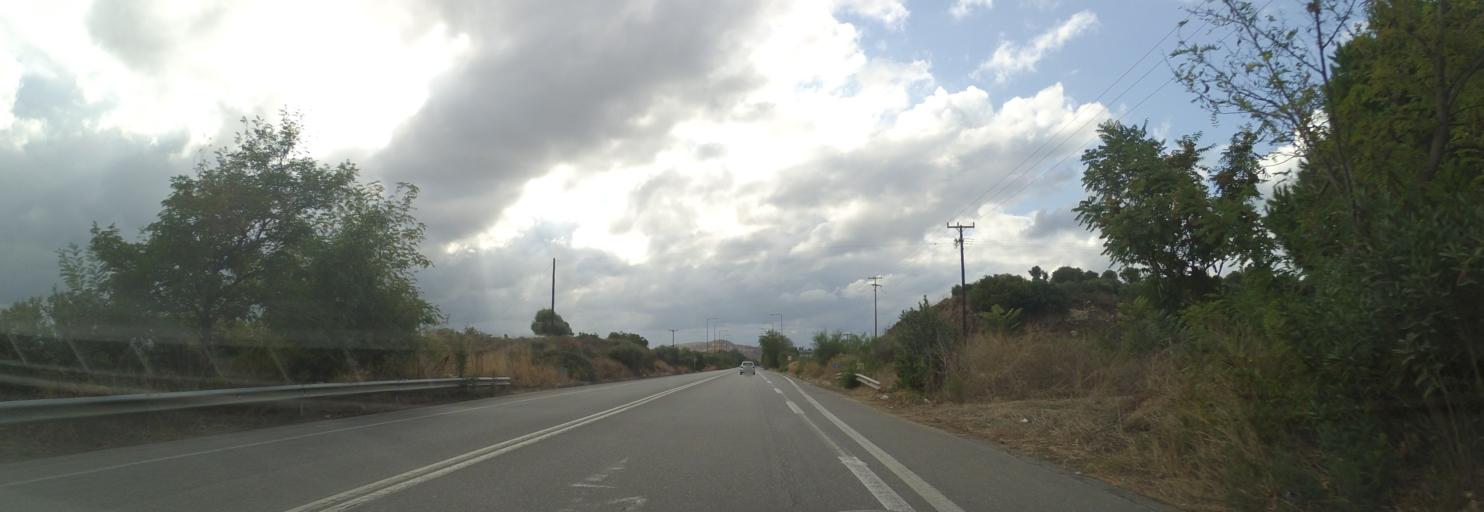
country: GR
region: Crete
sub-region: Nomos Rethymnis
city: Panormos
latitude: 35.4148
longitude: 24.7017
